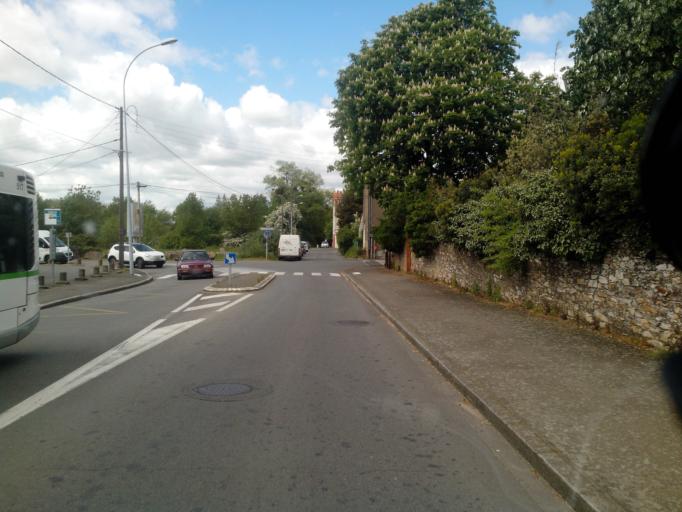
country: FR
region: Pays de la Loire
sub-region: Departement de la Loire-Atlantique
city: Reze
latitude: 47.1911
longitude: -1.5841
